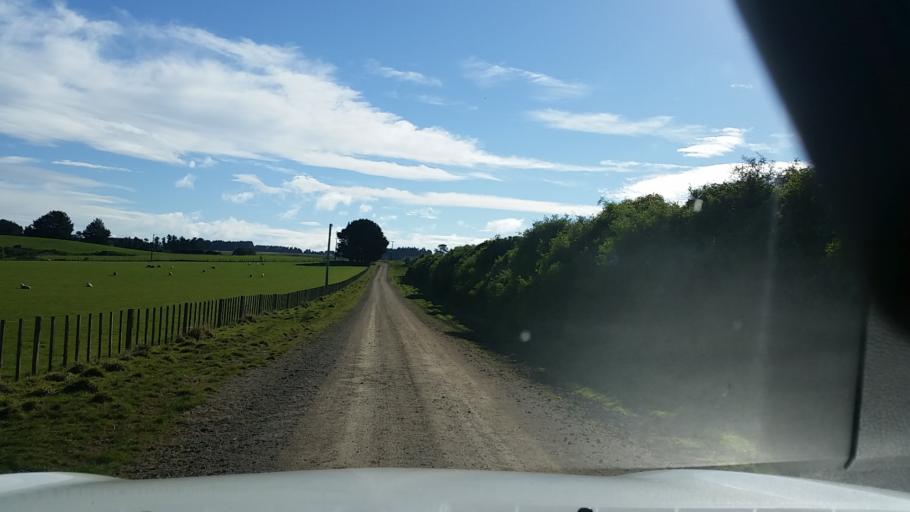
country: NZ
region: Taranaki
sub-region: South Taranaki District
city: Patea
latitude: -39.7021
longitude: 174.6323
